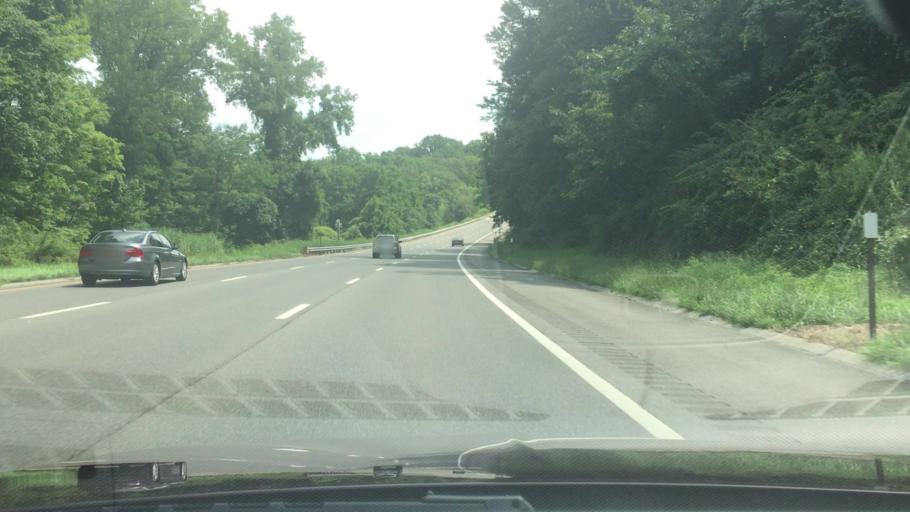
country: US
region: New York
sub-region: Westchester County
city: Yorktown Heights
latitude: 41.2244
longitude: -73.8139
